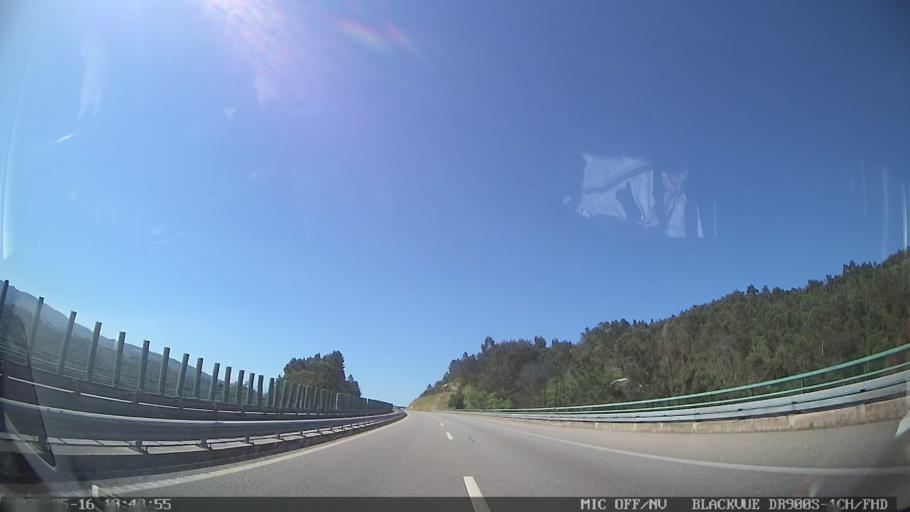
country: PT
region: Porto
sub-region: Amarante
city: Amarante
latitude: 41.2386
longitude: -8.1211
